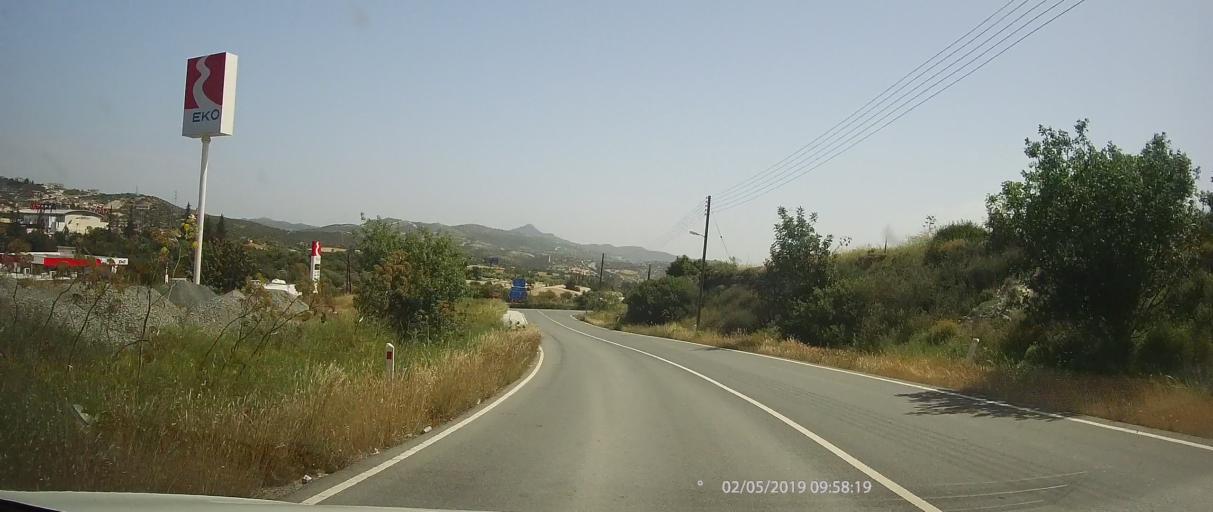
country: CY
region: Larnaka
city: Kofinou
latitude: 34.8139
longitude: 33.3608
